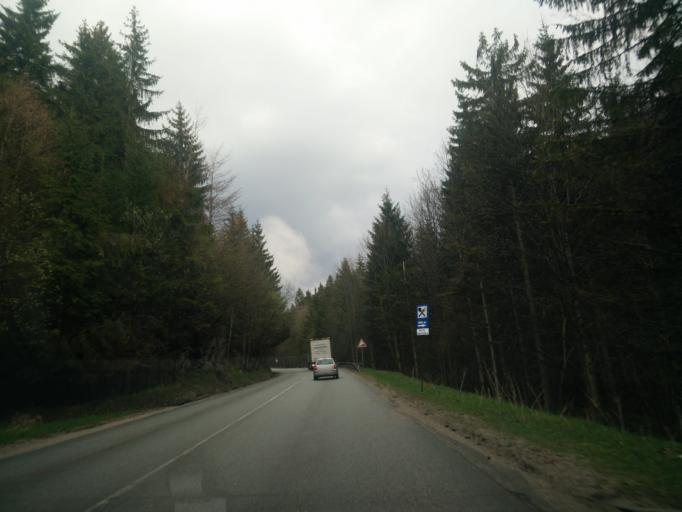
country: SK
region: Banskobystricky
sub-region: Okres Ziar nad Hronom
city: Kremnica
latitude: 48.8387
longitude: 18.9568
